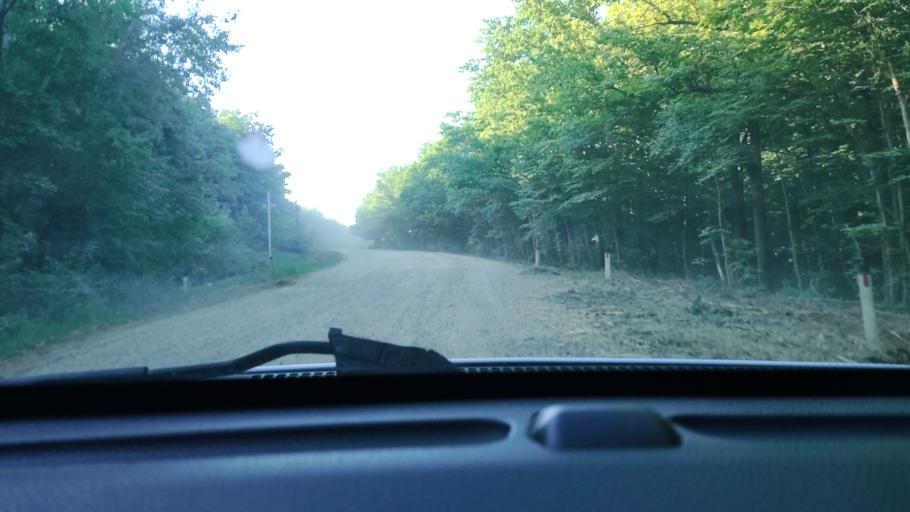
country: RU
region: Krasnodarskiy
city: Goryachiy Klyuch
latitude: 44.7143
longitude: 38.9913
